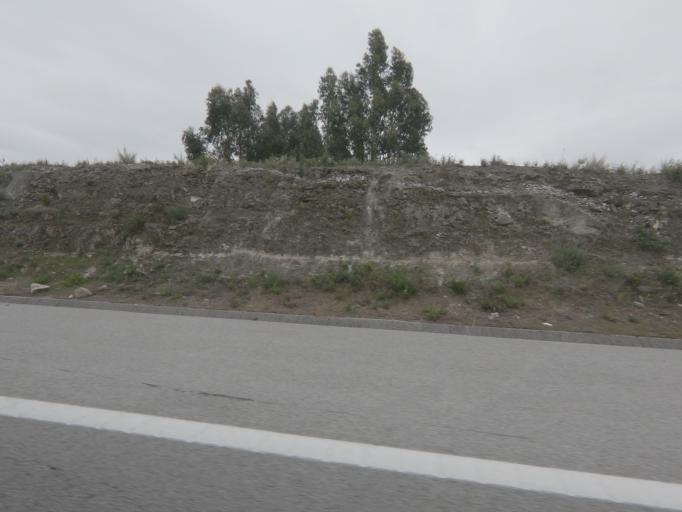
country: PT
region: Guarda
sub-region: Fornos de Algodres
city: Fornos de Algodres
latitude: 40.6063
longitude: -7.5526
